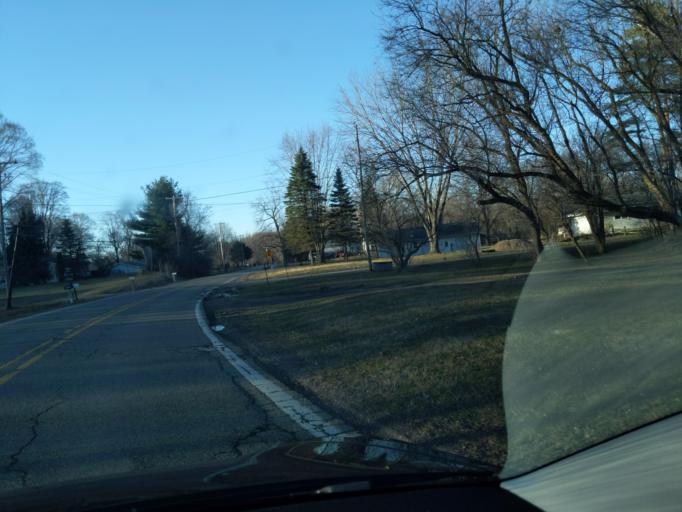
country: US
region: Michigan
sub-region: Livingston County
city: Pinckney
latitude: 42.4266
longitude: -84.0564
